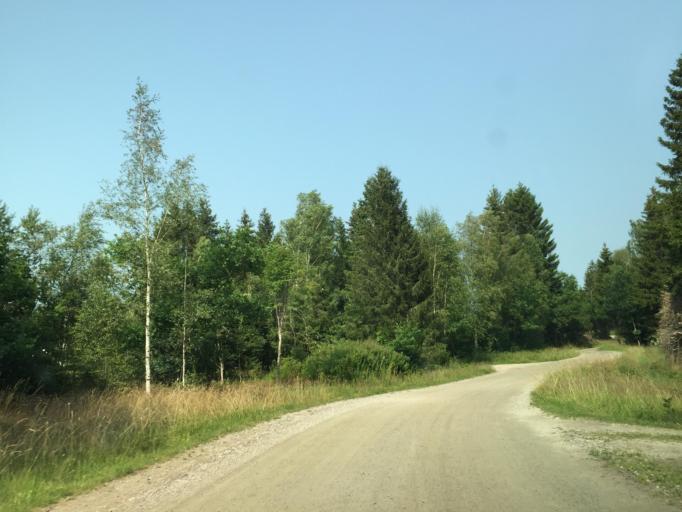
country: SE
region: Vaestra Goetaland
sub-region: Lilla Edets Kommun
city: Lilla Edet
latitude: 58.2560
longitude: 12.0933
